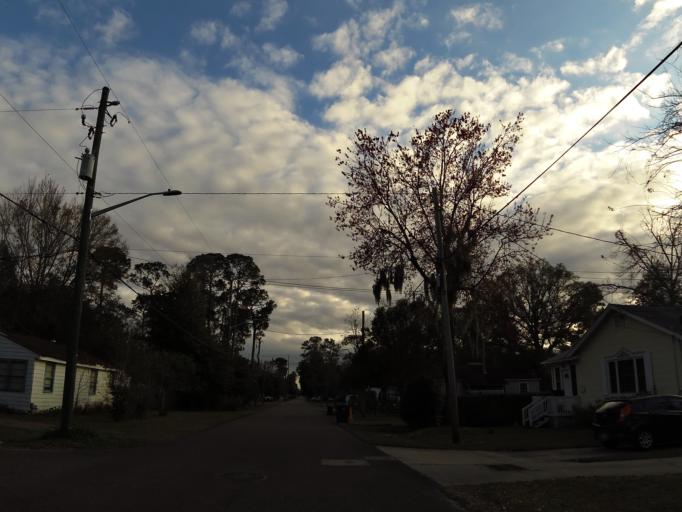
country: US
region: Florida
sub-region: Duval County
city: Jacksonville
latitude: 30.3054
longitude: -81.7263
